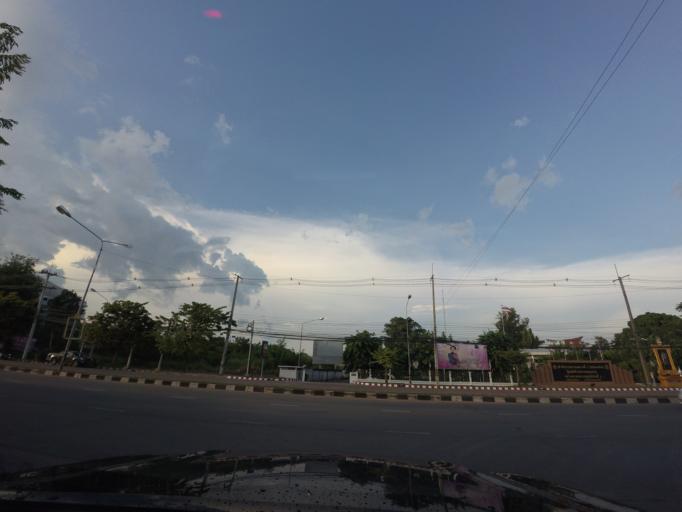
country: TH
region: Khon Kaen
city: Khon Kaen
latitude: 16.4279
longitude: 102.8606
